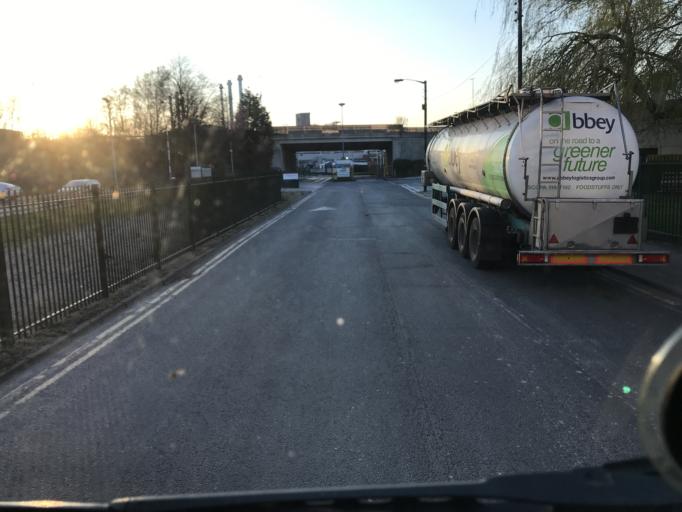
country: GB
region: England
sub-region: City and Borough of Salford
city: Eccles
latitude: 53.4771
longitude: -2.3234
